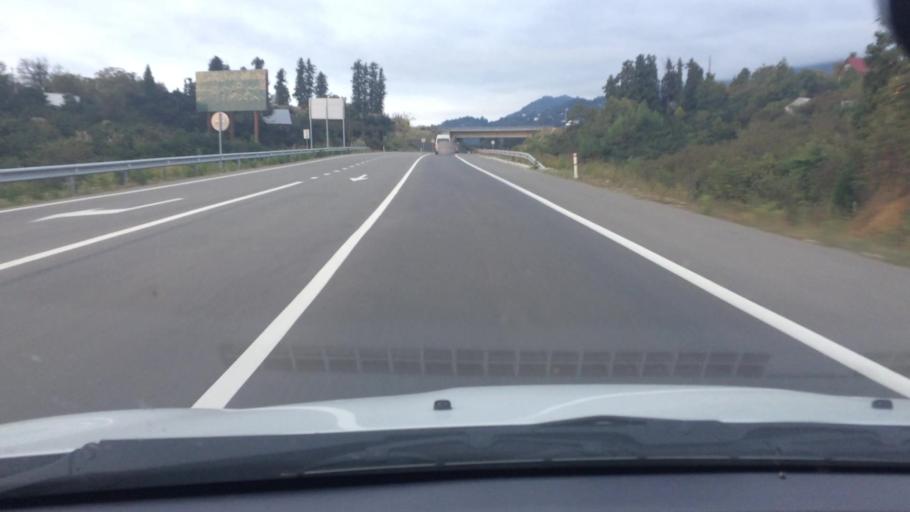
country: GE
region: Ajaria
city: Makhinjauri
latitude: 41.7050
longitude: 41.7393
